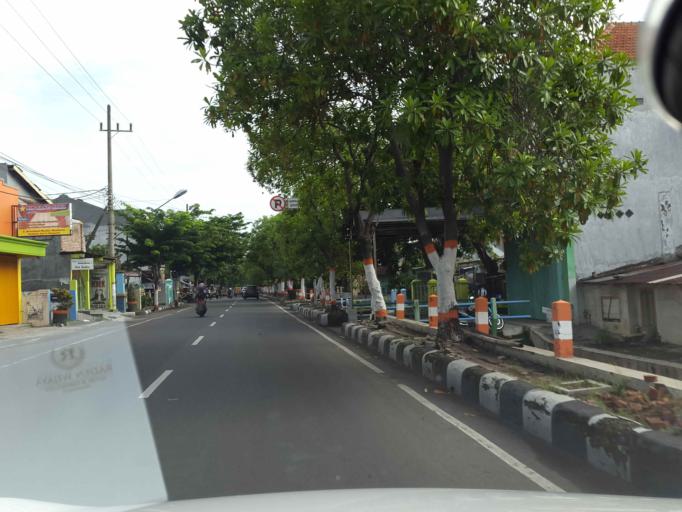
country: ID
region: East Java
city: Soko
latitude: -7.4783
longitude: 112.4288
